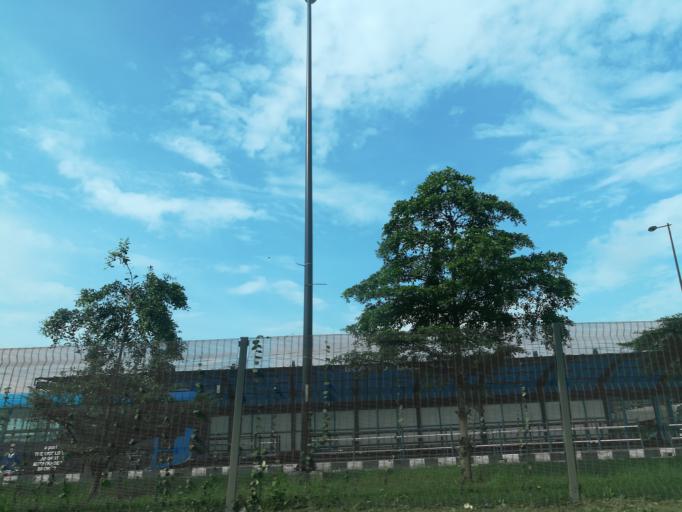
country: NG
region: Lagos
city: Ojota
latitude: 6.6102
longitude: 3.4211
